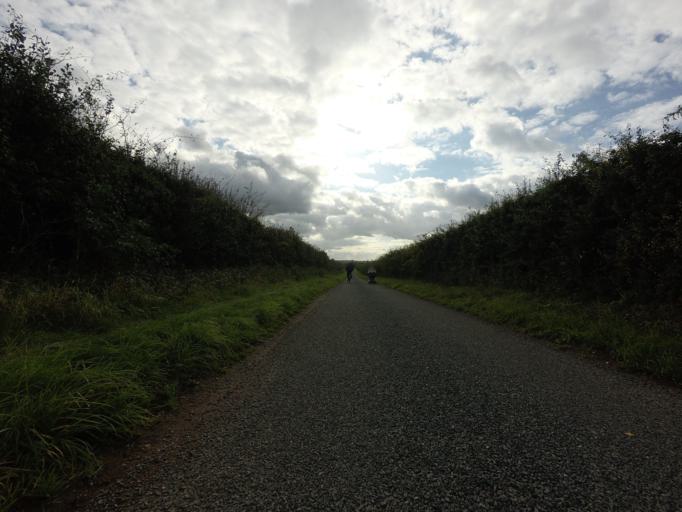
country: GB
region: England
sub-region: Norfolk
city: Dersingham
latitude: 52.8520
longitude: 0.5135
